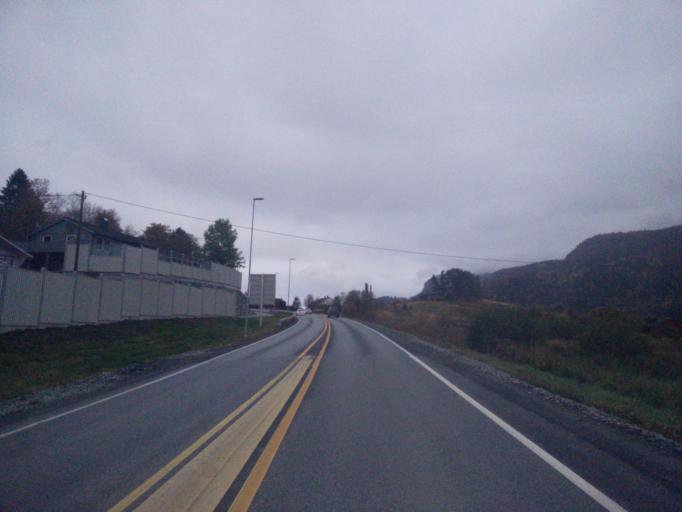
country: NO
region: Nord-Trondelag
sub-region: Stjordal
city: Stjordal
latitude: 63.4939
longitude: 10.8836
